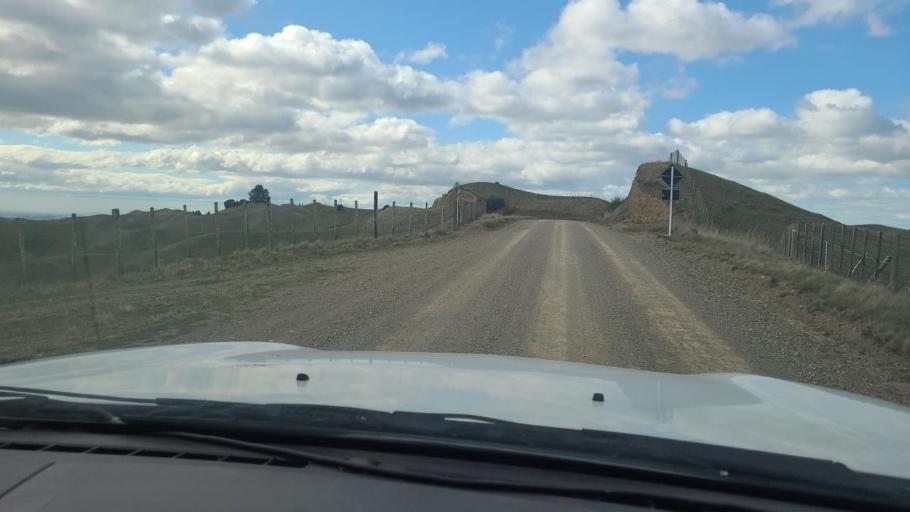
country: NZ
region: Hawke's Bay
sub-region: Hastings District
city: Hastings
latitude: -39.6857
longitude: 176.4619
